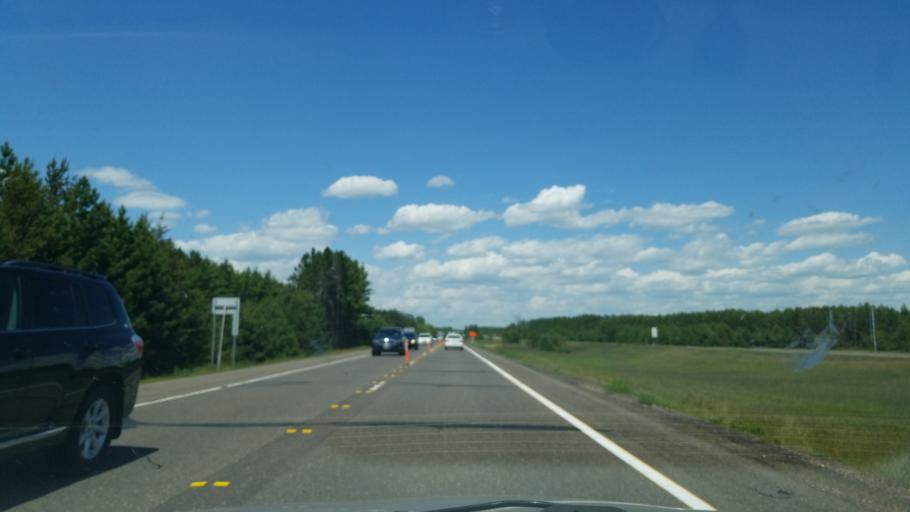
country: US
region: Minnesota
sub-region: Carlton County
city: Moose Lake
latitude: 46.3246
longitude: -92.8253
